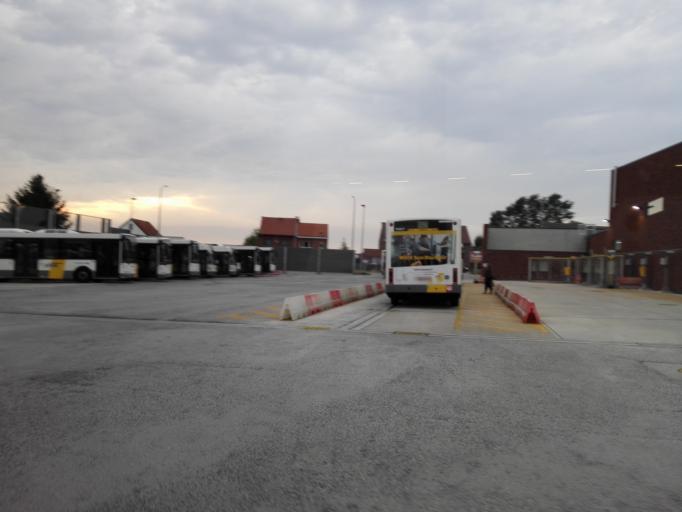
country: BE
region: Flanders
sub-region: Provincie Vlaams-Brabant
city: Glabbeek-Zuurbemde
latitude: 50.9199
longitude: 4.9112
